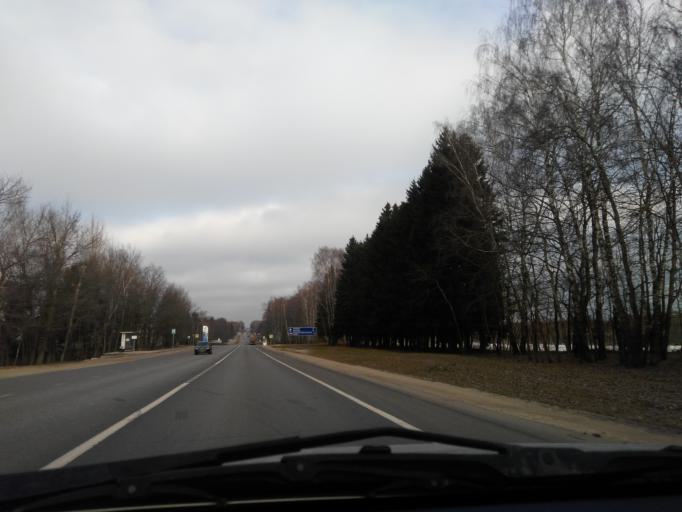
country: RU
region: Moskovskaya
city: Aprelevka
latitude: 55.2843
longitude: 37.1218
